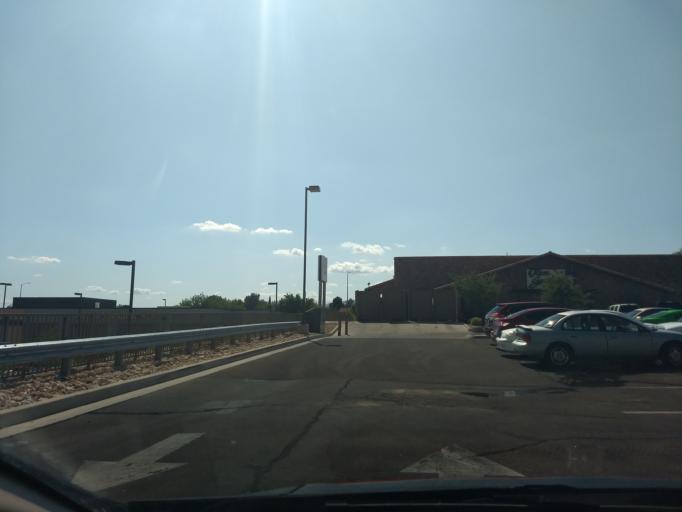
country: US
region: Utah
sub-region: Washington County
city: Saint George
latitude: 37.1046
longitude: -113.5543
